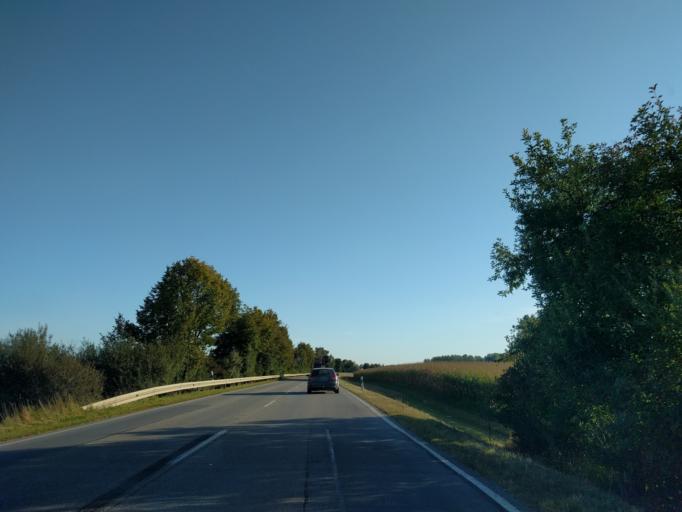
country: DE
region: Bavaria
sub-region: Lower Bavaria
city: Osterhofen
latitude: 48.7022
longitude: 13.0457
